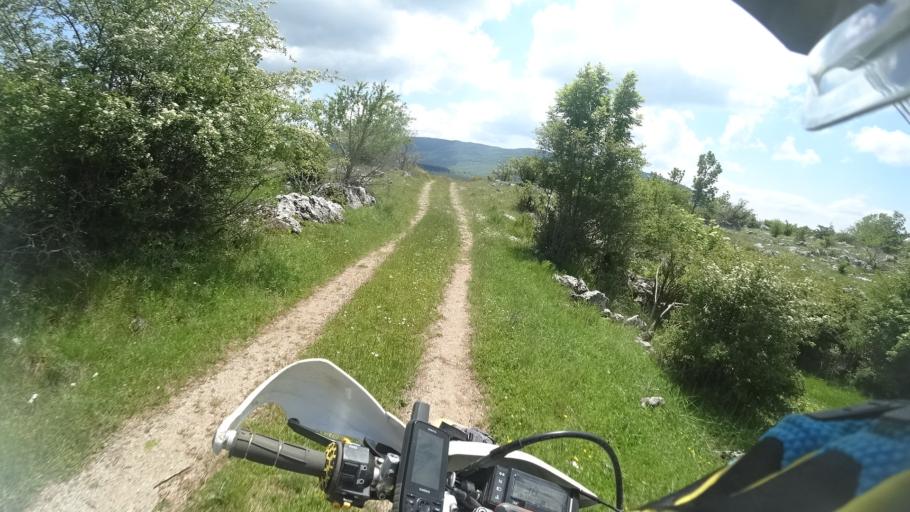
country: HR
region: Zadarska
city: Gracac
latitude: 44.3648
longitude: 15.9461
